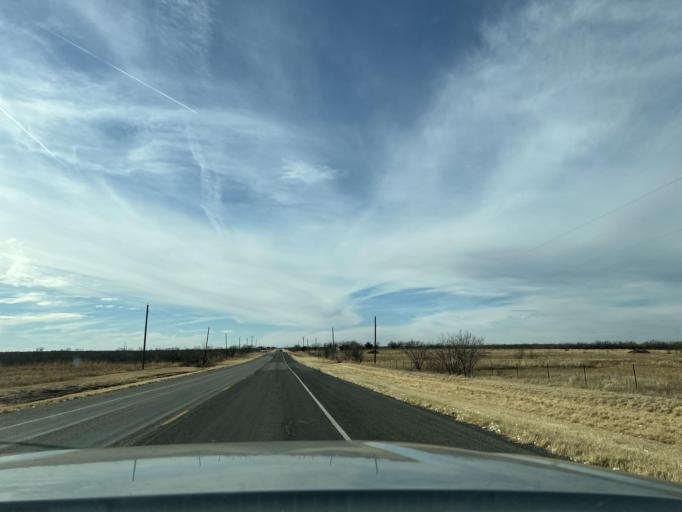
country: US
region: Texas
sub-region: Jones County
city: Anson
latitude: 32.7519
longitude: -99.9254
